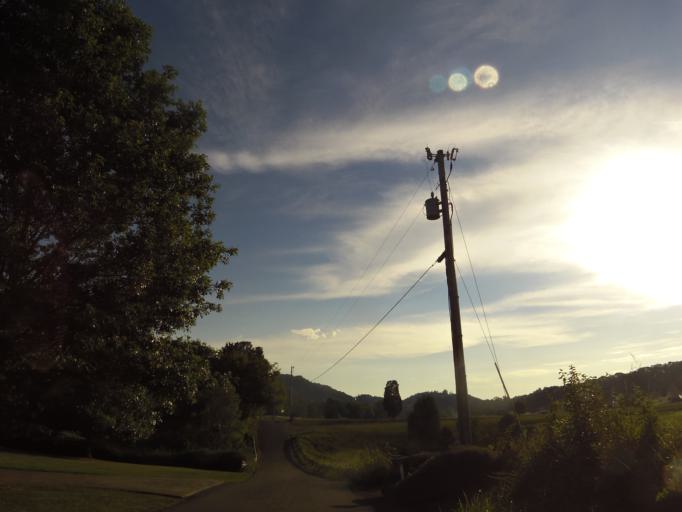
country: US
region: Tennessee
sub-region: Blount County
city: Wildwood
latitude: 35.8540
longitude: -83.8980
